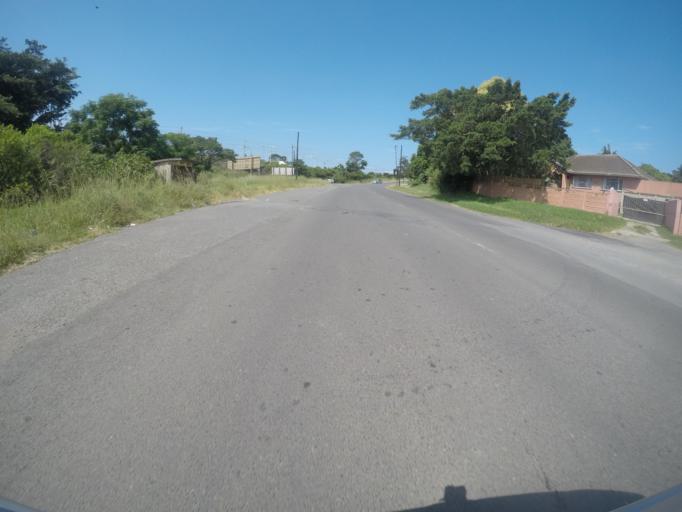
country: ZA
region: Eastern Cape
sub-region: Buffalo City Metropolitan Municipality
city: East London
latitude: -32.9721
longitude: 27.8784
